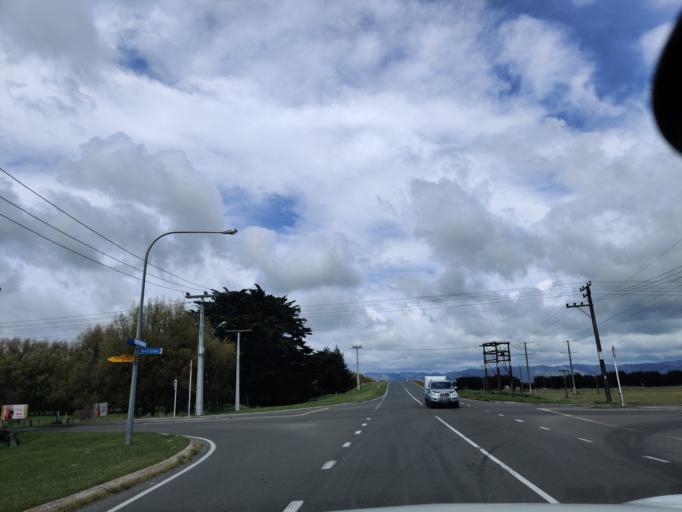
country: NZ
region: Manawatu-Wanganui
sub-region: Palmerston North City
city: Palmerston North
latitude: -40.3653
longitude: 175.5516
